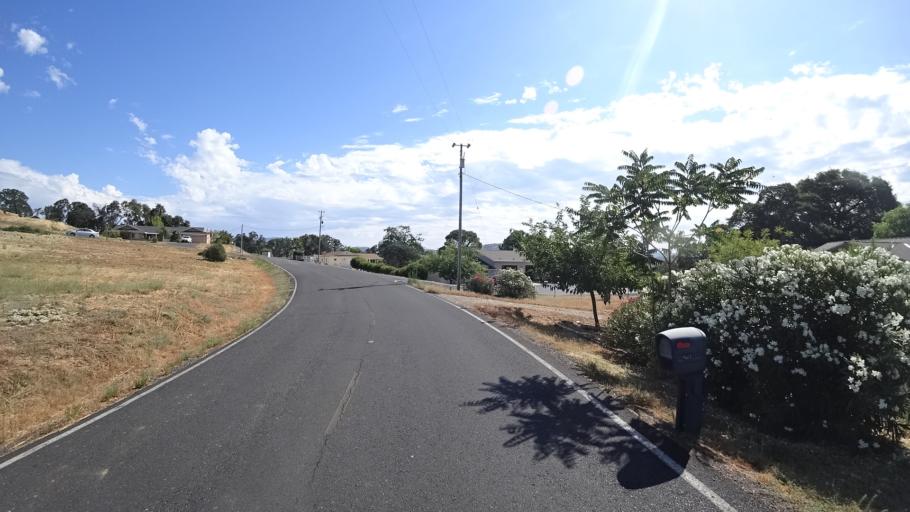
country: US
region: California
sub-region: Calaveras County
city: Copperopolis
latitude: 37.9355
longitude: -120.6393
